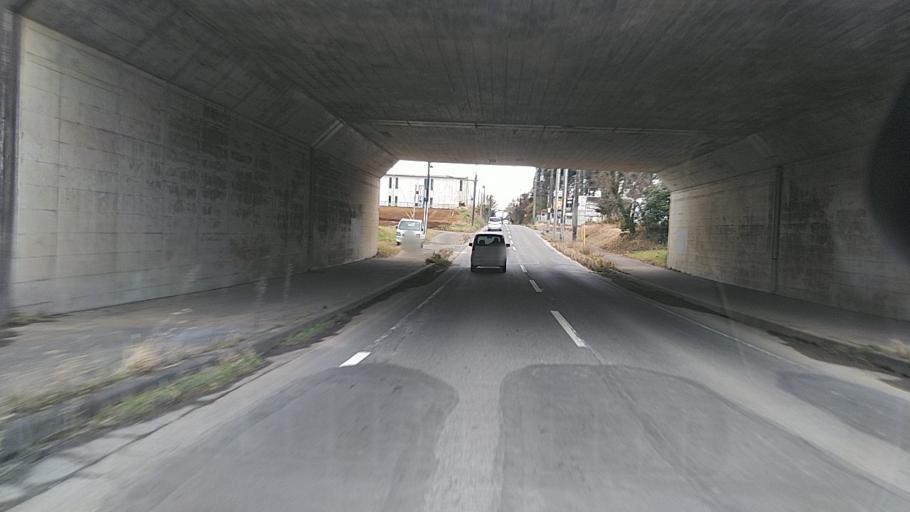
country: JP
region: Chiba
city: Sawara
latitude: 35.8393
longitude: 140.4553
